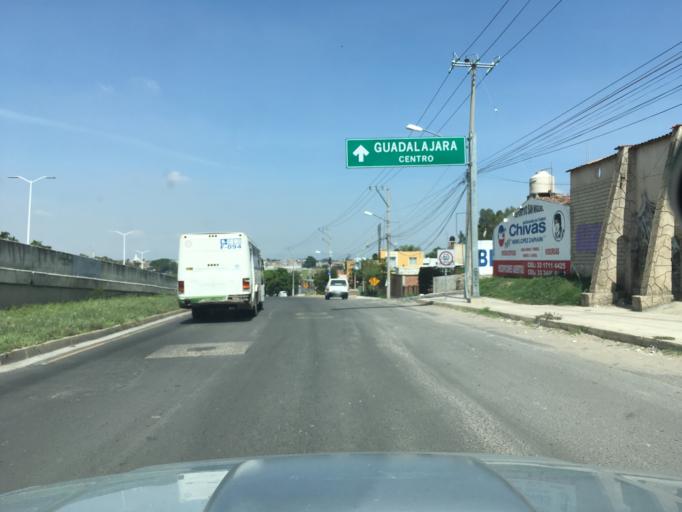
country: MX
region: Jalisco
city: Tonala
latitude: 20.6847
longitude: -103.2473
